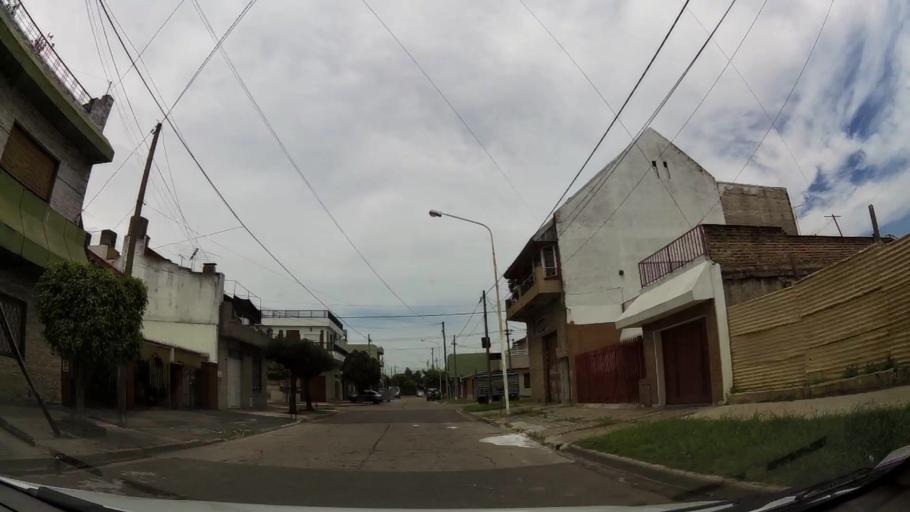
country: AR
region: Buenos Aires
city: San Justo
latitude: -34.6704
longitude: -58.5474
